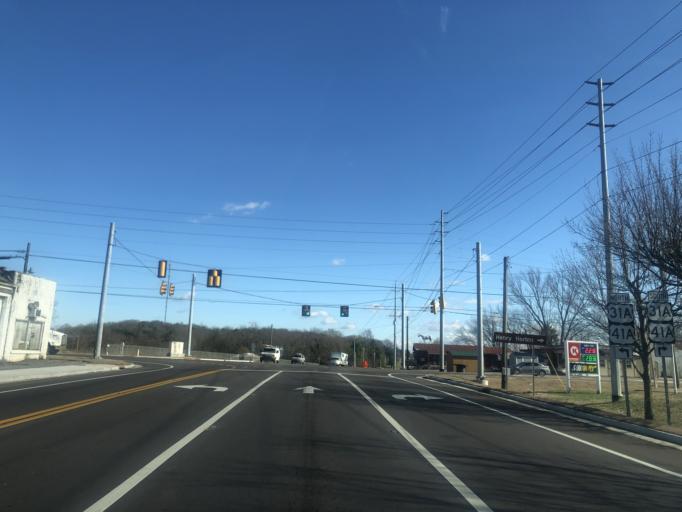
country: US
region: Tennessee
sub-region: Williamson County
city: Nolensville
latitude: 35.8544
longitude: -86.6597
